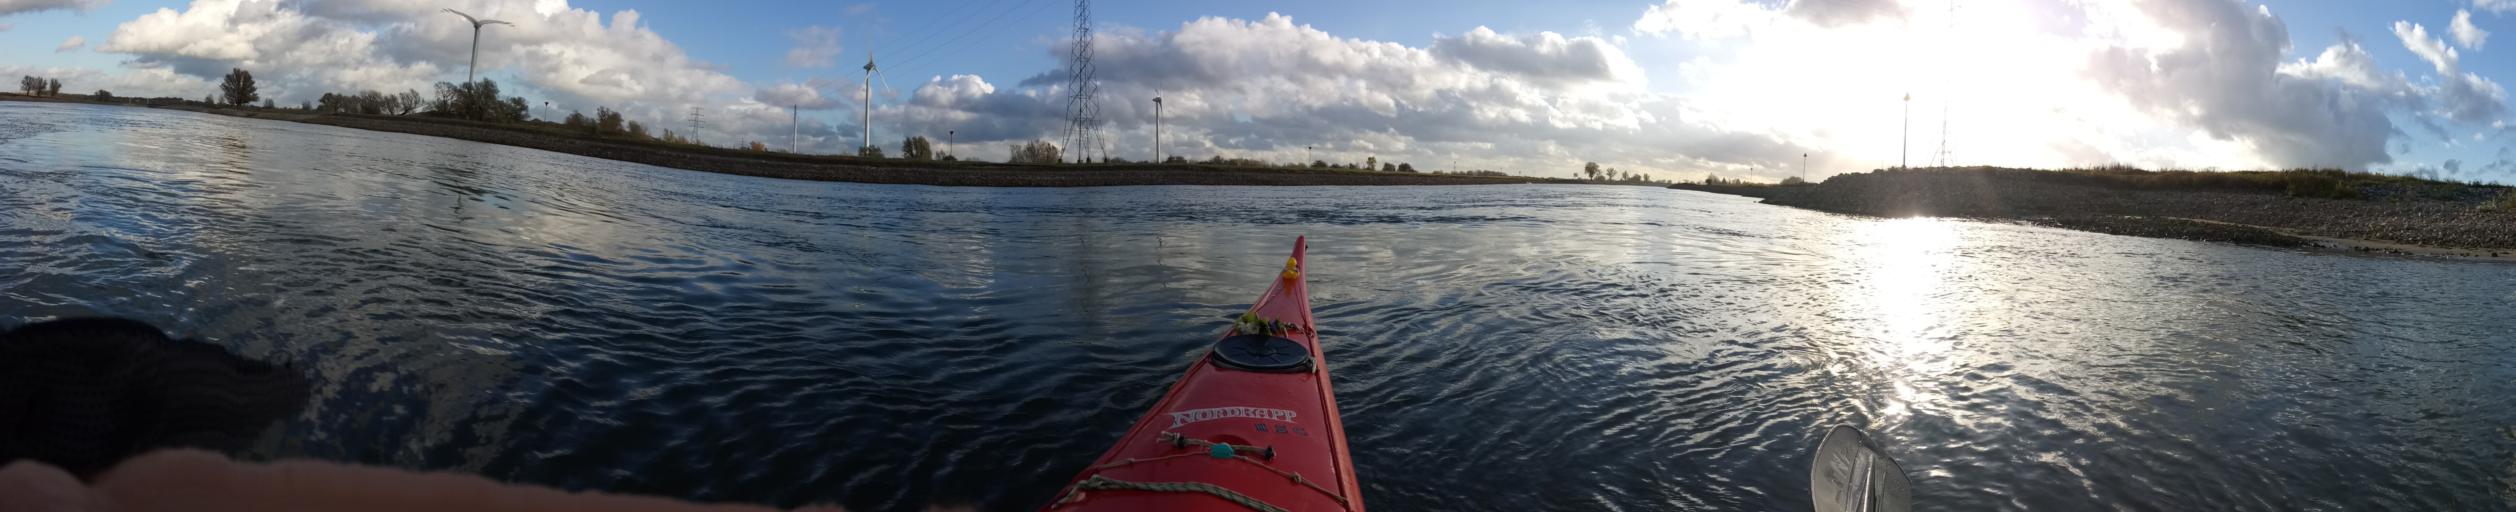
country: NL
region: Gelderland
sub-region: Gemeente Zutphen
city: Zutphen
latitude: 52.1635
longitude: 6.1852
